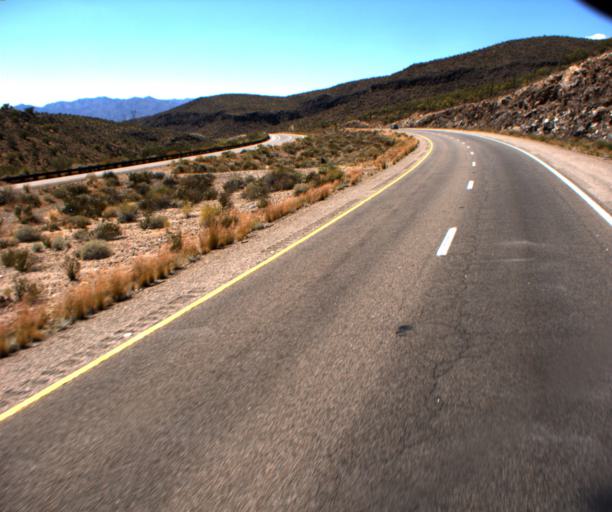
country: US
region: Arizona
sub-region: Yavapai County
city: Bagdad
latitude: 34.5665
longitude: -113.4586
